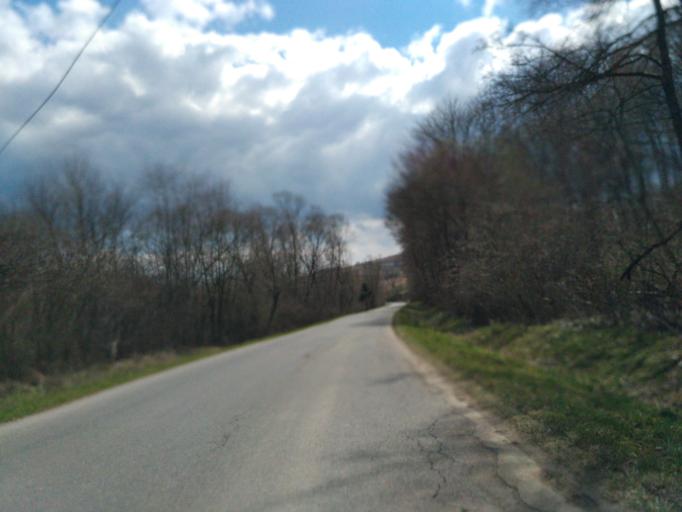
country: PL
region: Subcarpathian Voivodeship
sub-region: Powiat sanocki
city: Tyrawa Woloska
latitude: 49.5850
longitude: 22.3448
